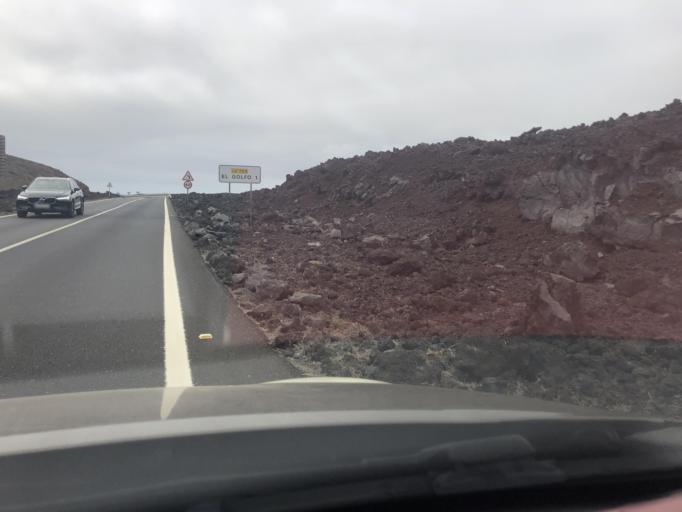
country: ES
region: Canary Islands
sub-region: Provincia de Las Palmas
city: Yaiza
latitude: 28.9790
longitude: -13.8207
